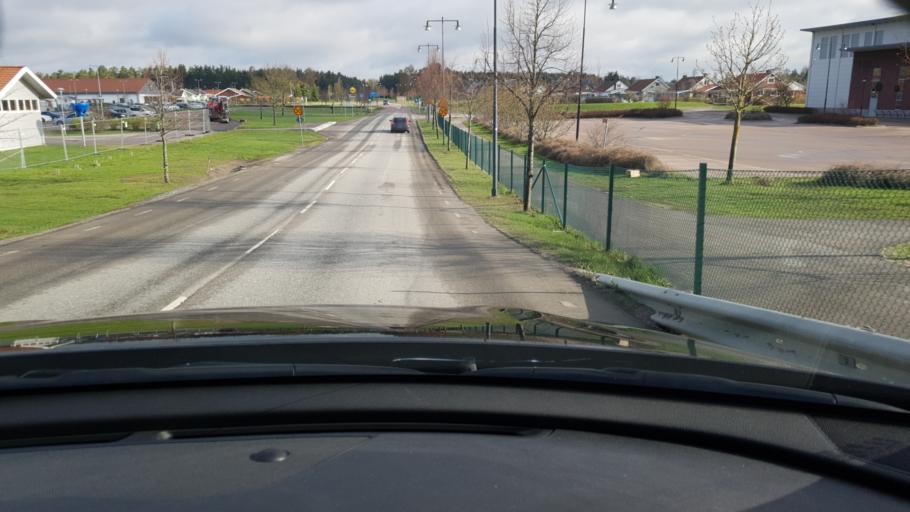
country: SE
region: Vaestmanland
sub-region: Arboga Kommun
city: Arboga
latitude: 59.3999
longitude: 15.8322
